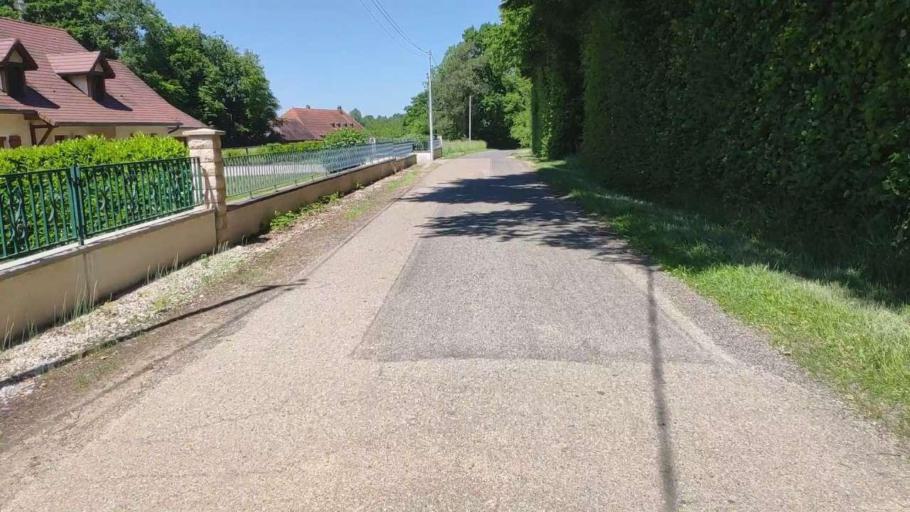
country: FR
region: Franche-Comte
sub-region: Departement du Jura
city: Bletterans
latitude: 46.7461
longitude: 5.4121
